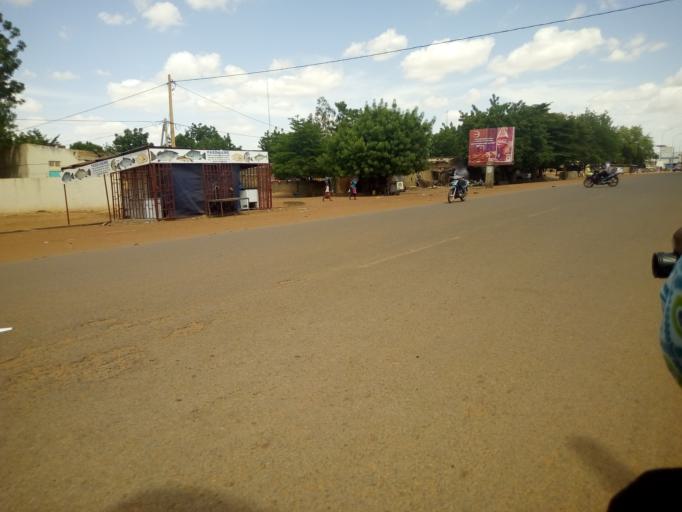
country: ML
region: Segou
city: Segou
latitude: 13.4361
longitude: -6.2647
